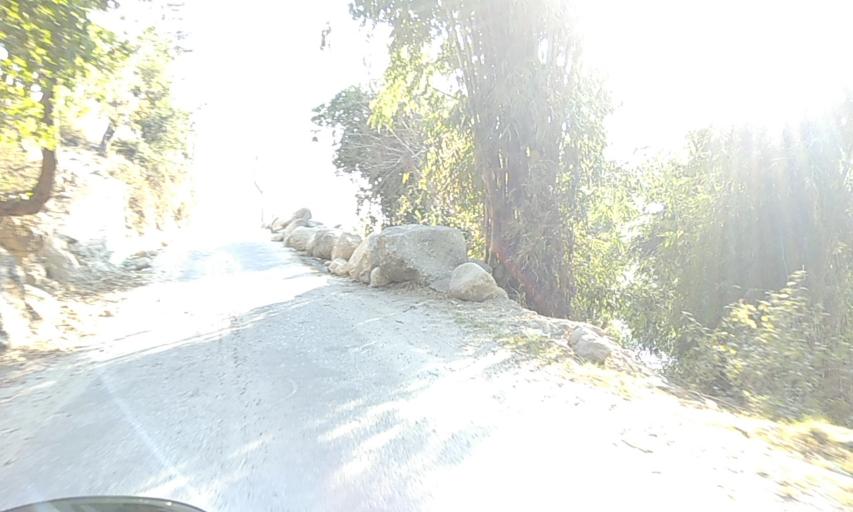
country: IN
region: Himachal Pradesh
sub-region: Kangra
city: Palampur
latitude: 32.1347
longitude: 76.5353
